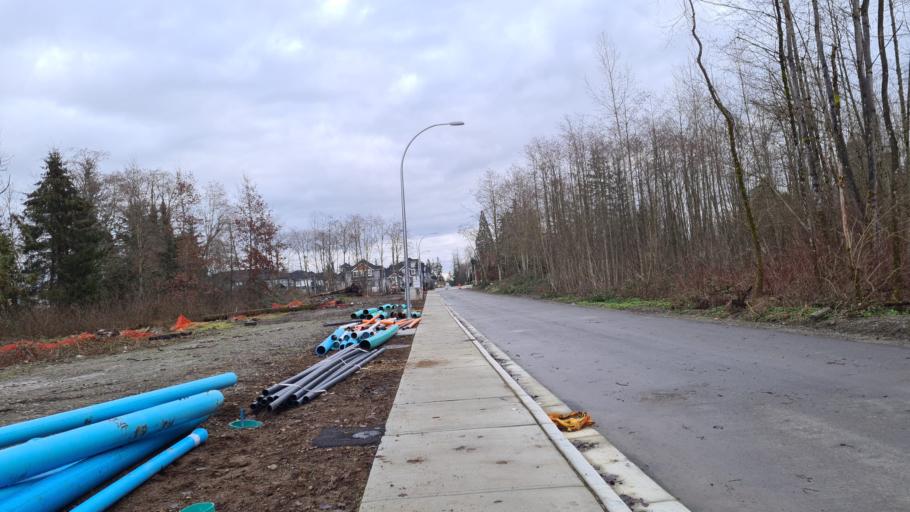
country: CA
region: British Columbia
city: Walnut Grove
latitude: 49.1408
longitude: -122.6484
